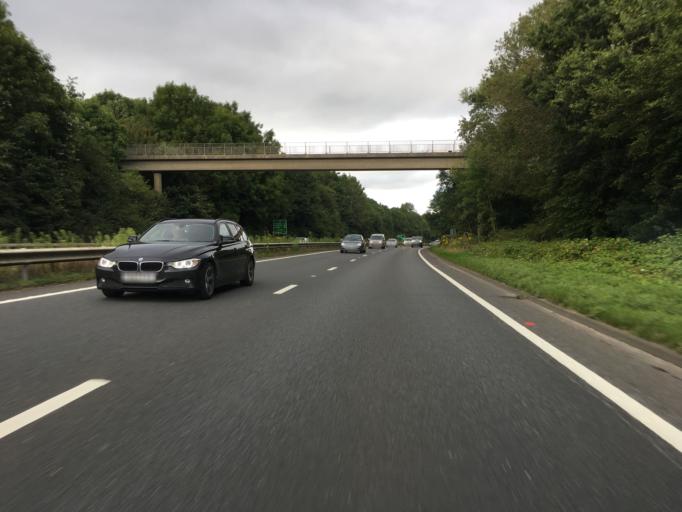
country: GB
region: England
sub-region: Hampshire
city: Petersfield
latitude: 51.0130
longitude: -0.9510
